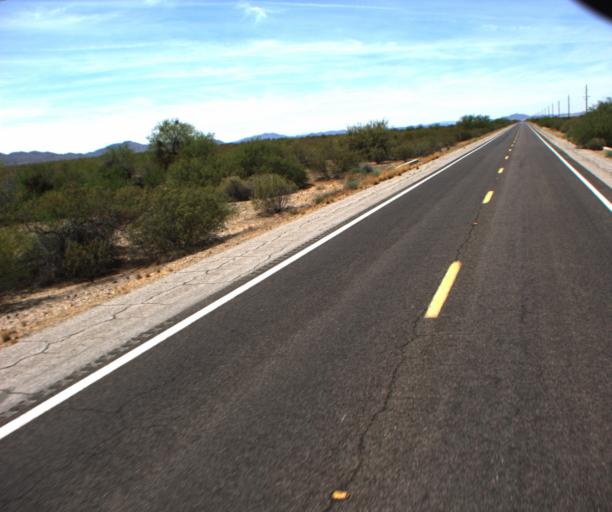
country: US
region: Arizona
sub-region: La Paz County
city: Salome
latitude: 33.8562
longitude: -113.4338
